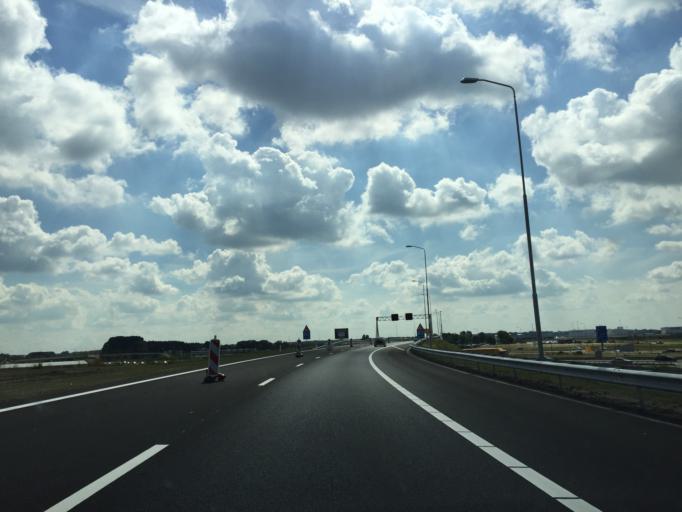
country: NL
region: North Holland
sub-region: Gemeente Aalsmeer
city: Aalsmeer
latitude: 52.3269
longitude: 4.7782
